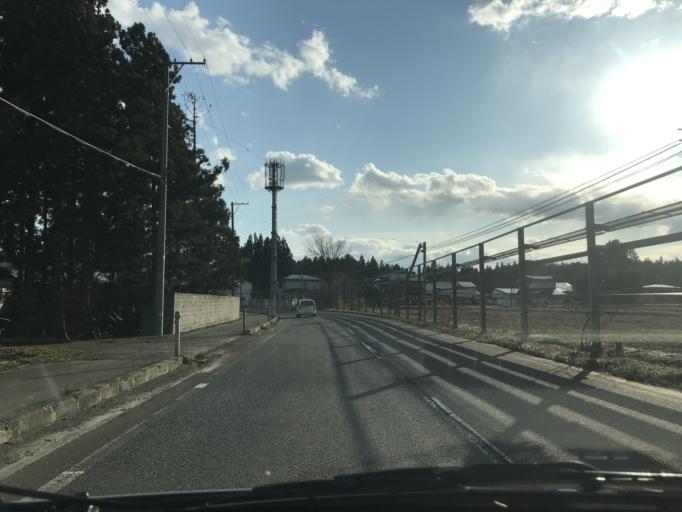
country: JP
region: Iwate
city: Kitakami
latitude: 39.3249
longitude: 141.0381
